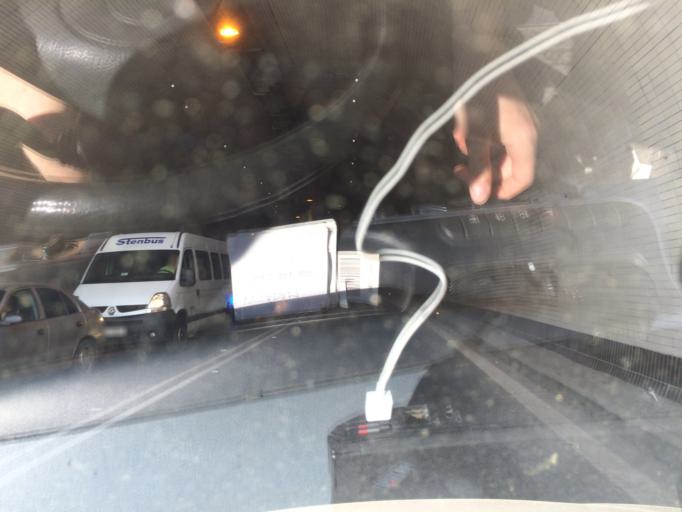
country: CZ
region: Praha
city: Prague
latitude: 50.0956
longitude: 14.4267
